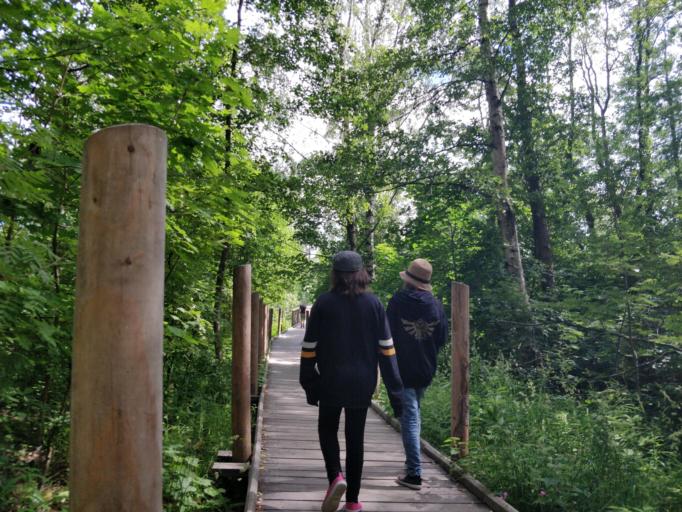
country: FI
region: Uusimaa
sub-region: Helsinki
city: Helsinki
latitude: 60.2129
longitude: 24.9875
